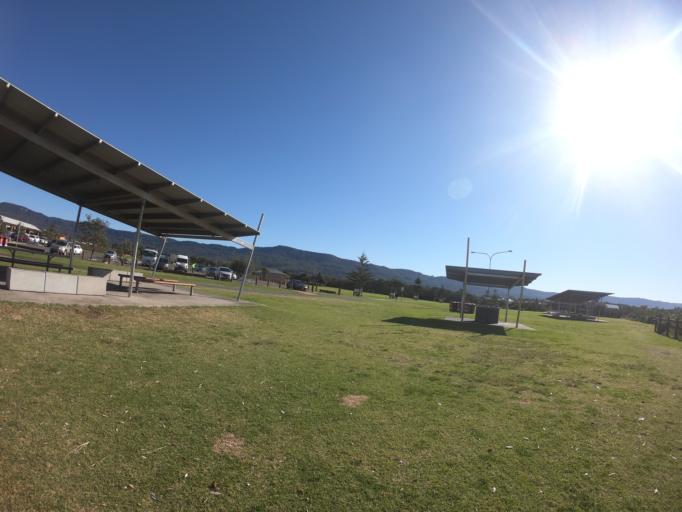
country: AU
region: New South Wales
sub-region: Wollongong
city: East Corrimal
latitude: -34.3847
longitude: 150.9149
